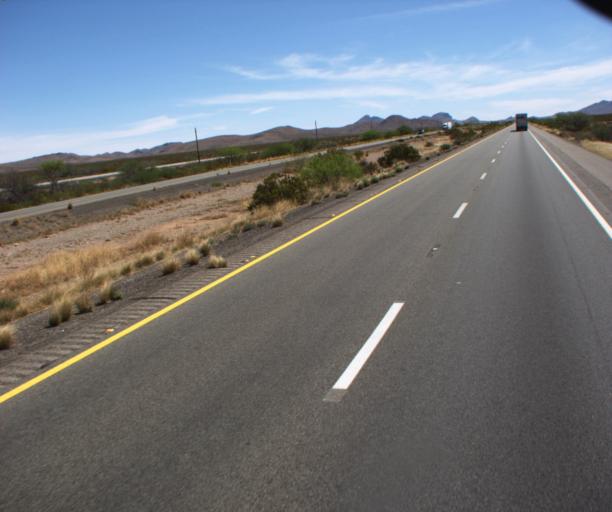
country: US
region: New Mexico
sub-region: Hidalgo County
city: Lordsburg
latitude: 32.2470
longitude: -109.1340
